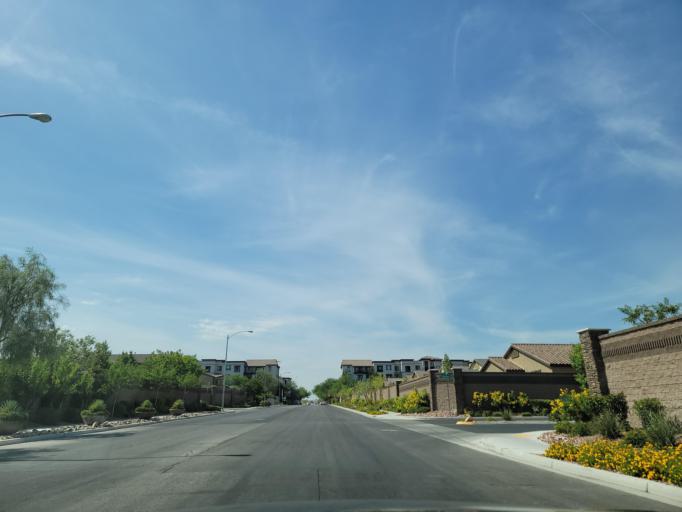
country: US
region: Nevada
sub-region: Clark County
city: Spring Valley
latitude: 36.0758
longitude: -115.2840
